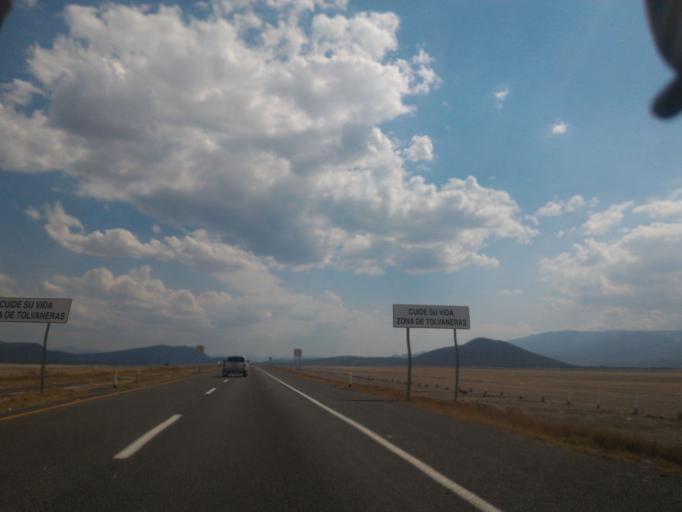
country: MX
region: Jalisco
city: Zacoalco de Torres
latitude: 20.3044
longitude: -103.5602
